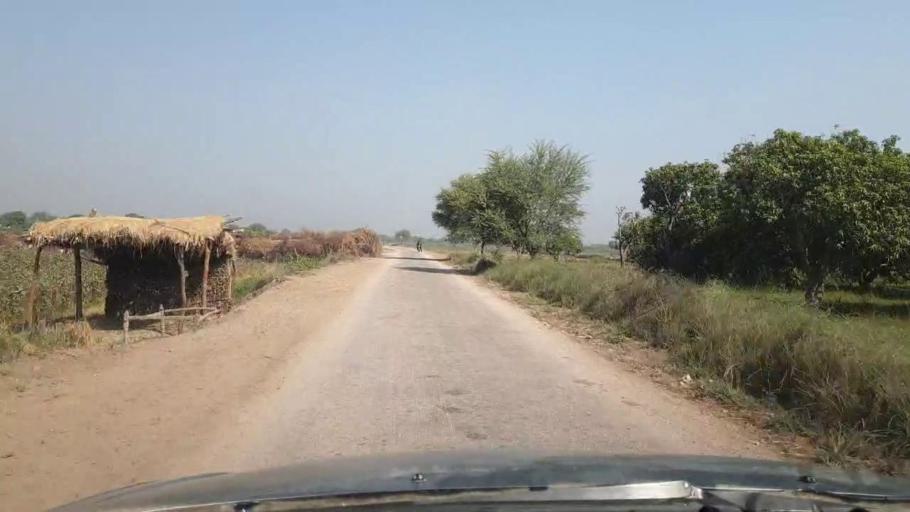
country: PK
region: Sindh
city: Tando Jam
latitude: 25.3161
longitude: 68.5400
